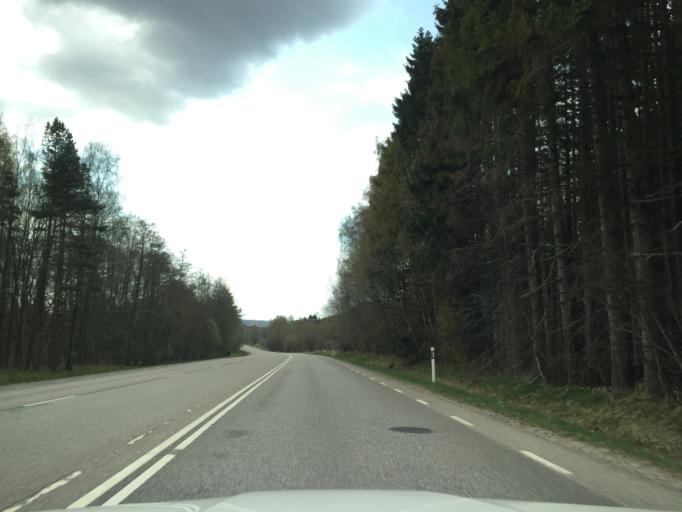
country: SE
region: Vaestra Goetaland
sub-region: Stenungsunds Kommun
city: Stora Hoga
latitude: 58.0500
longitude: 11.9009
